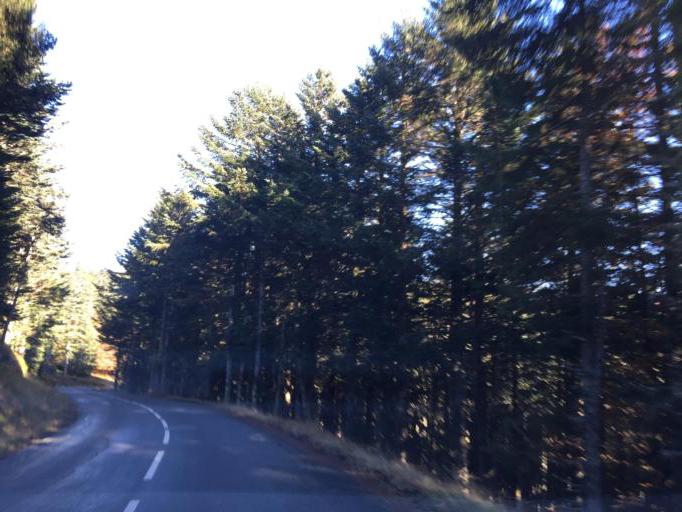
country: FR
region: Rhone-Alpes
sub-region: Departement de la Loire
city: Saint-Julien-Molin-Molette
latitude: 45.3780
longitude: 4.5633
